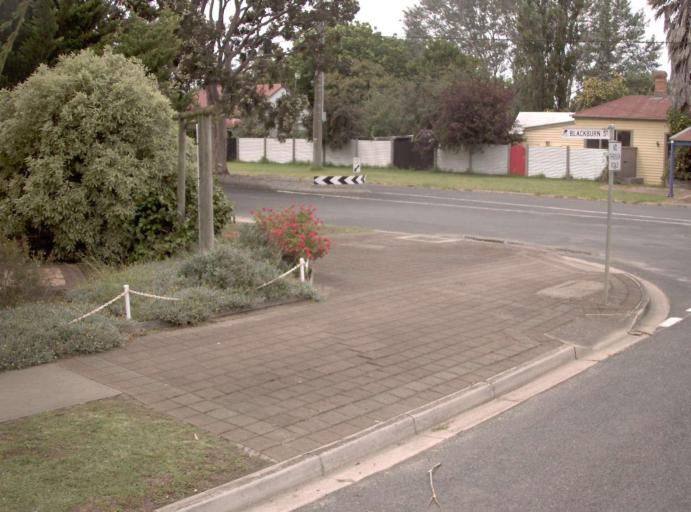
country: AU
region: Victoria
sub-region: Wellington
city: Sale
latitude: -37.9682
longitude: 147.0796
